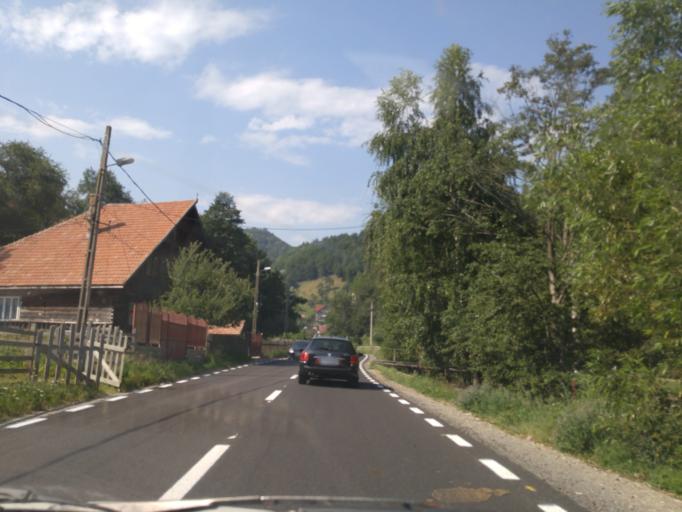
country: RO
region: Brasov
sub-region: Municipiul Brasov
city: Moeciu de Jos
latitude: 45.4777
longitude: 25.3128
